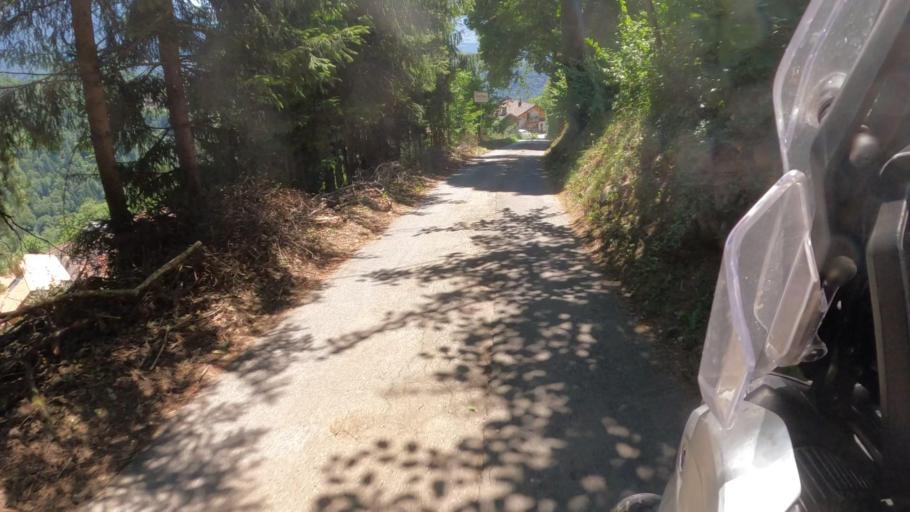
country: CH
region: Vaud
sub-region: Aigle District
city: Bex
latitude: 46.2815
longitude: 7.0237
